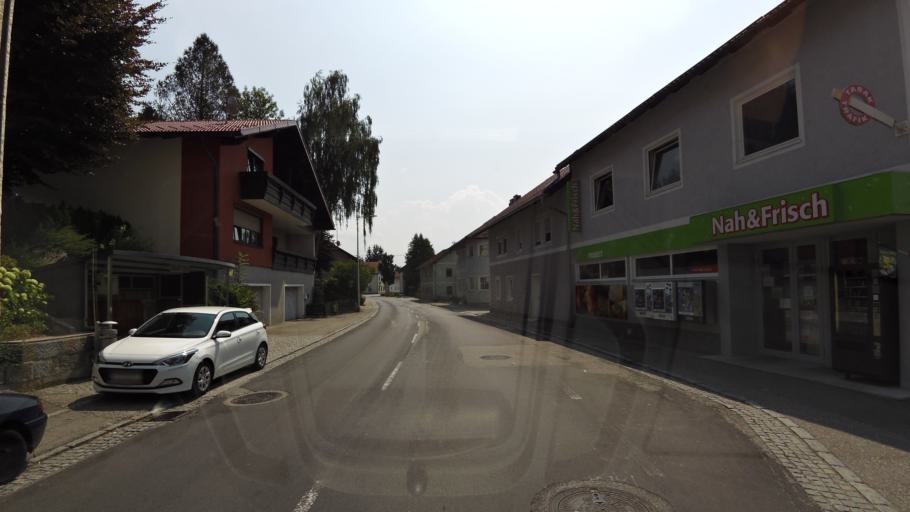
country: AT
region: Upper Austria
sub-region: Politischer Bezirk Braunau am Inn
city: Altheim
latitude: 48.2408
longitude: 13.3446
